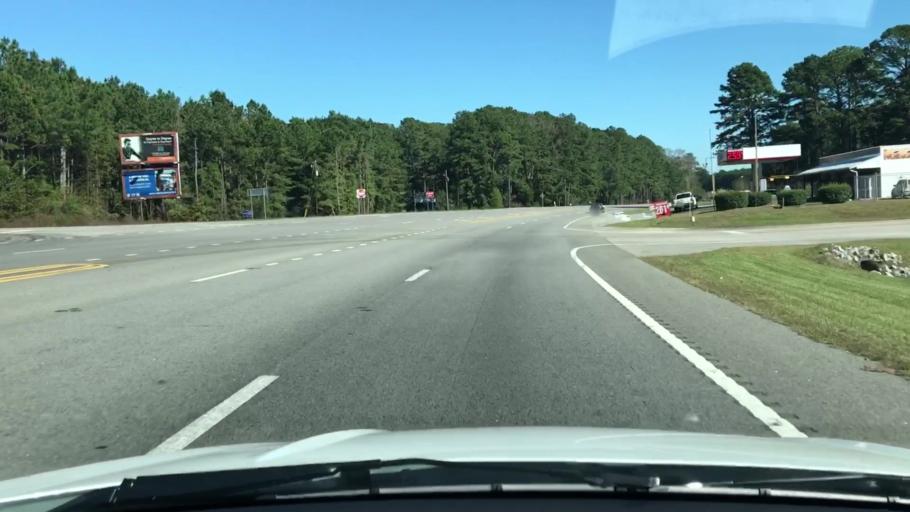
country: US
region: South Carolina
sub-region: Colleton County
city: Walterboro
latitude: 32.7369
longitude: -80.5880
